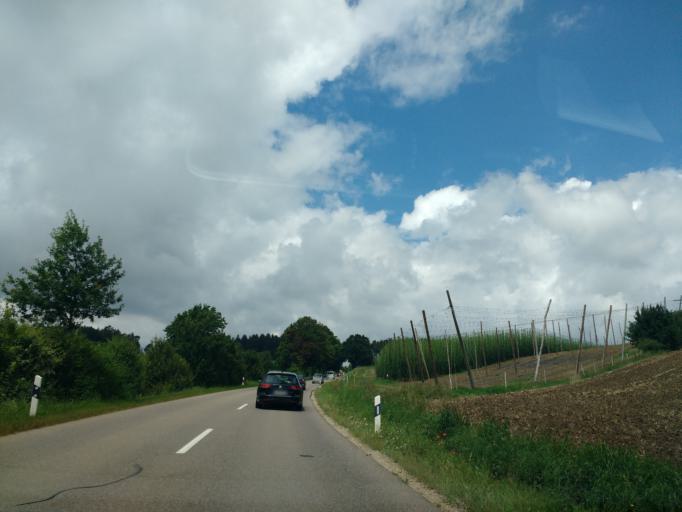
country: DE
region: Bavaria
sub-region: Upper Bavaria
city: Schweitenkirchen
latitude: 48.5547
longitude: 11.5857
